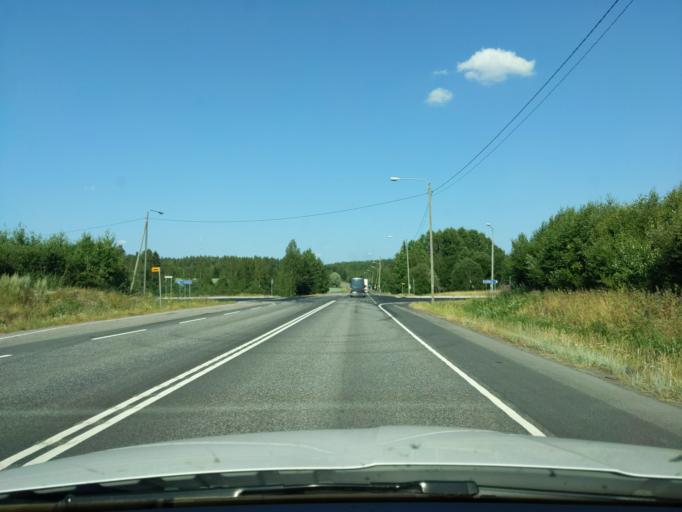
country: FI
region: Paijanne Tavastia
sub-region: Lahti
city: Hollola
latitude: 60.9491
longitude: 25.4223
